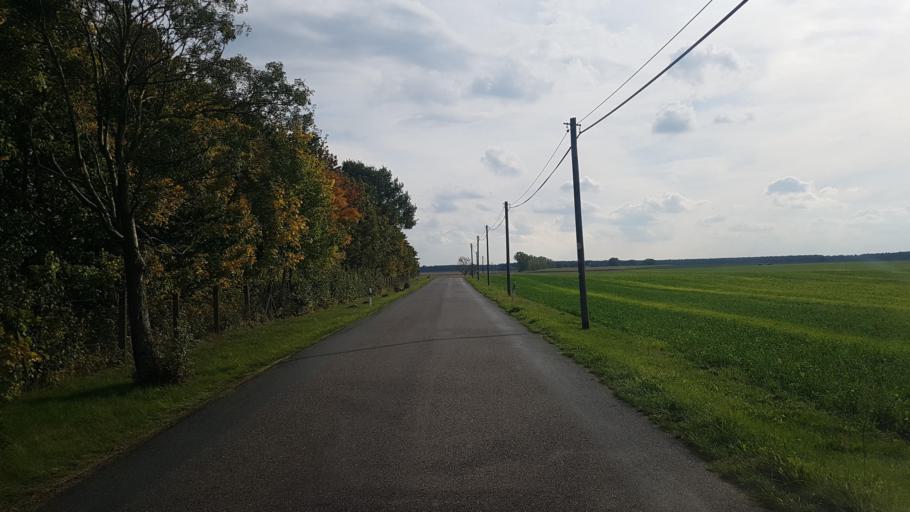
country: DE
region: Brandenburg
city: Dahme
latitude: 51.8767
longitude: 13.3829
